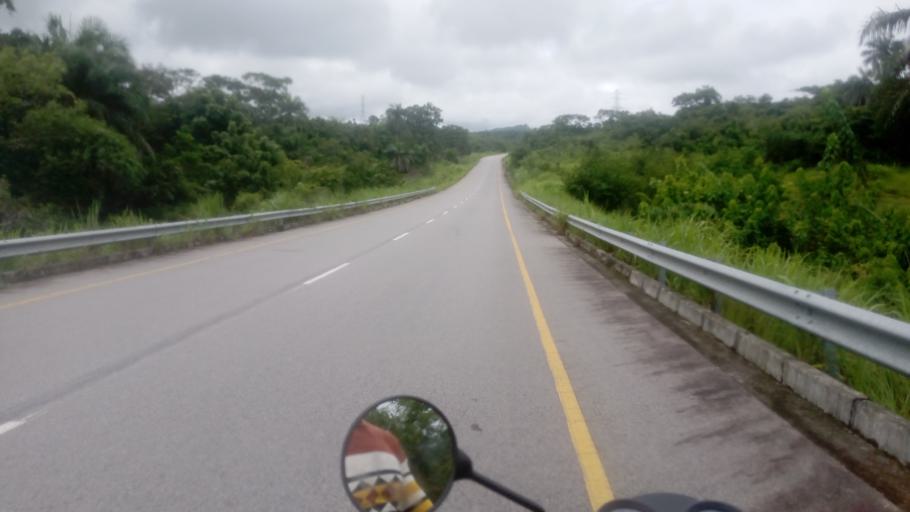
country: SL
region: Northern Province
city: Masaka
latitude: 8.6579
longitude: -11.7820
